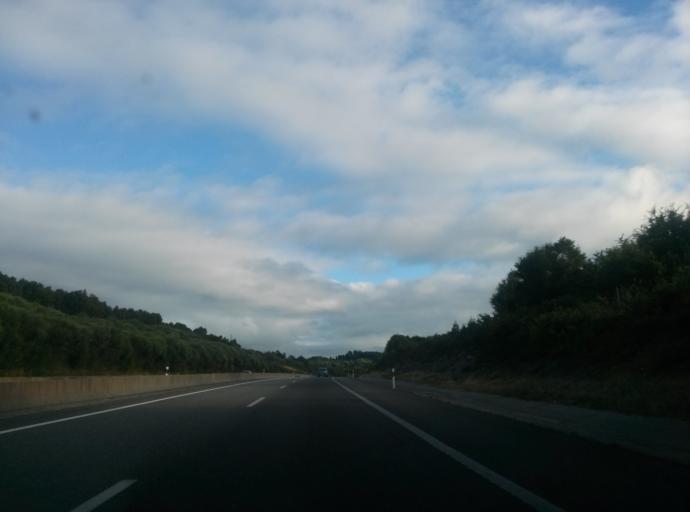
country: ES
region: Galicia
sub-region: Provincia de Lugo
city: Muras
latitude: 43.3837
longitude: -7.7771
